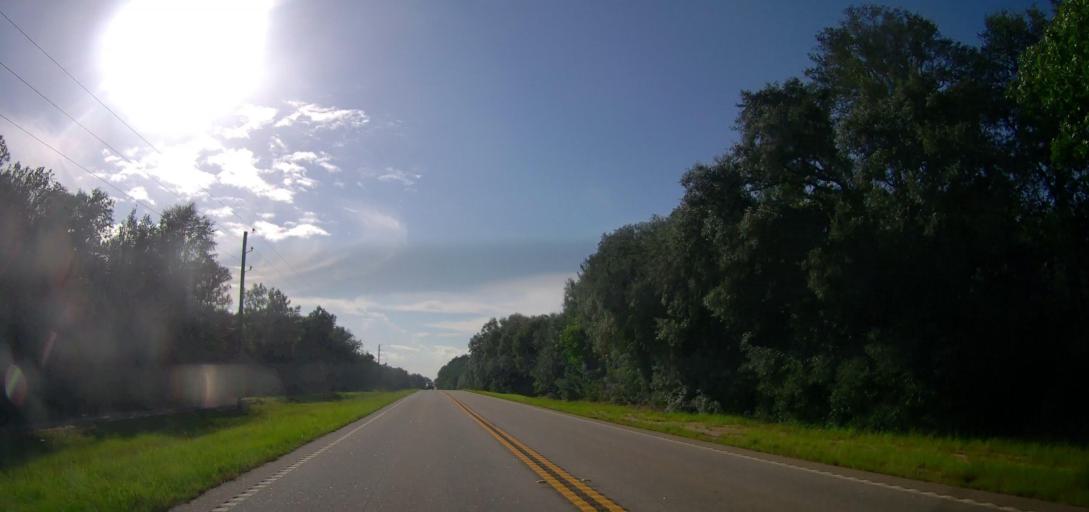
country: US
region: Georgia
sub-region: Coffee County
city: Douglas
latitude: 31.4630
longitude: -82.7534
